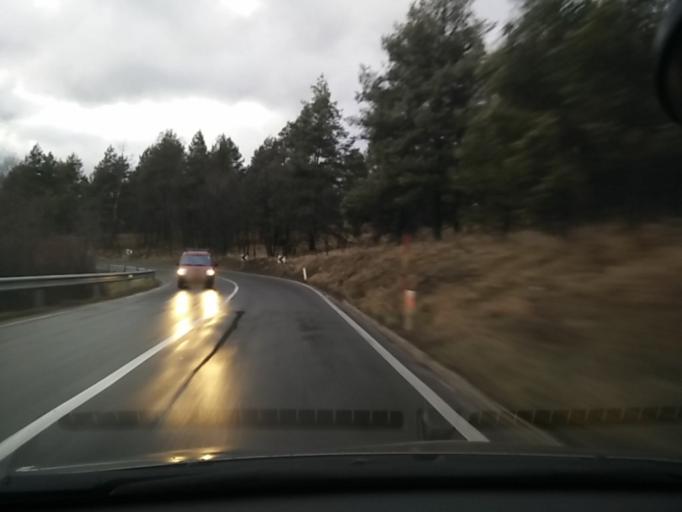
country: SI
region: Pivka
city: Pivka
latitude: 45.5276
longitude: 14.1302
